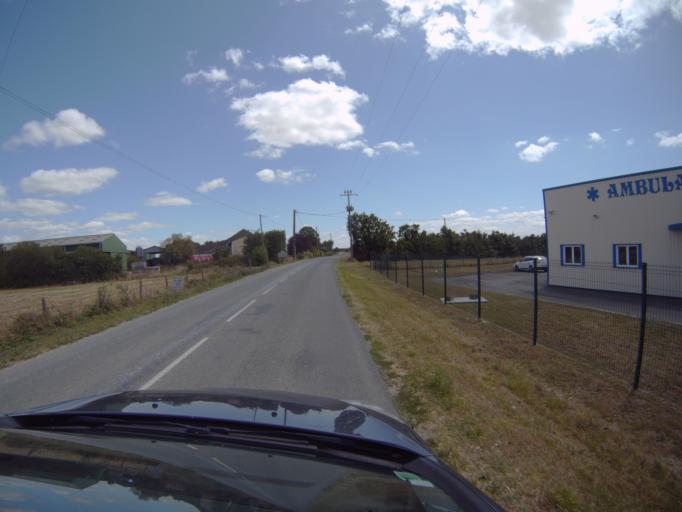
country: FR
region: Poitou-Charentes
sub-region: Departement de la Charente-Maritime
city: Saint-Jean-de-Liversay
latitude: 46.2647
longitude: -0.8734
